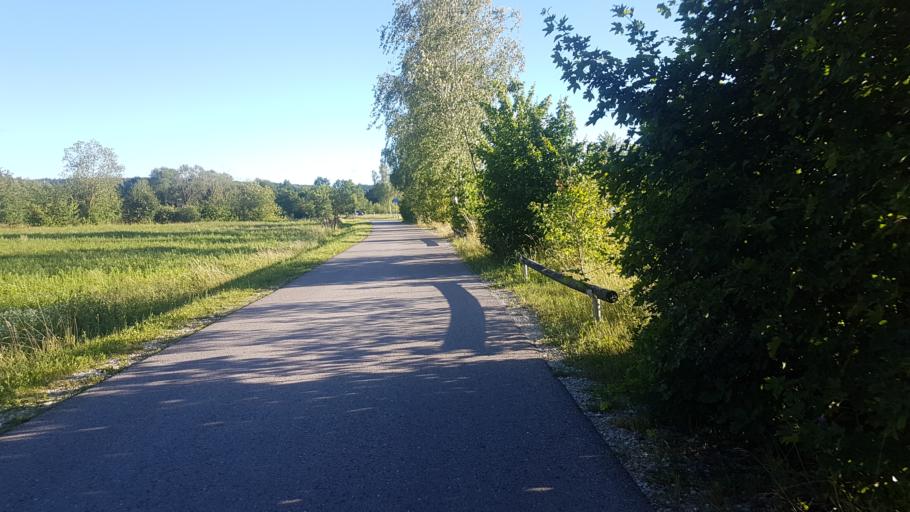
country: DE
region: Bavaria
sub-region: Regierungsbezirk Mittelfranken
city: Absberg
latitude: 49.1318
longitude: 10.8568
